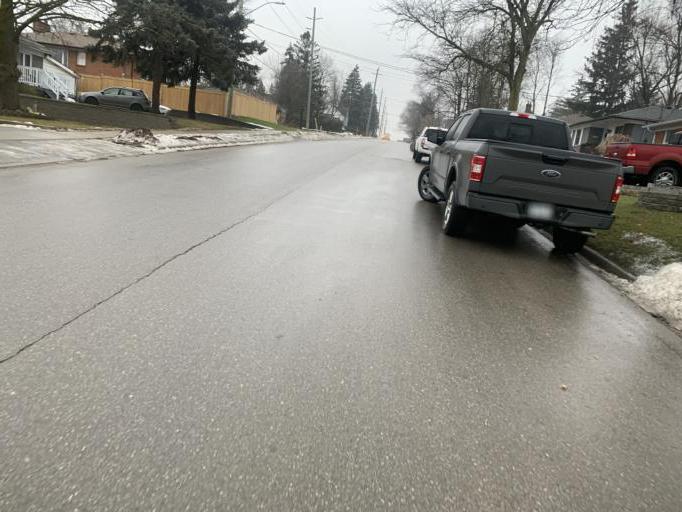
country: CA
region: Ontario
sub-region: Halton
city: Milton
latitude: 43.6558
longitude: -79.9292
